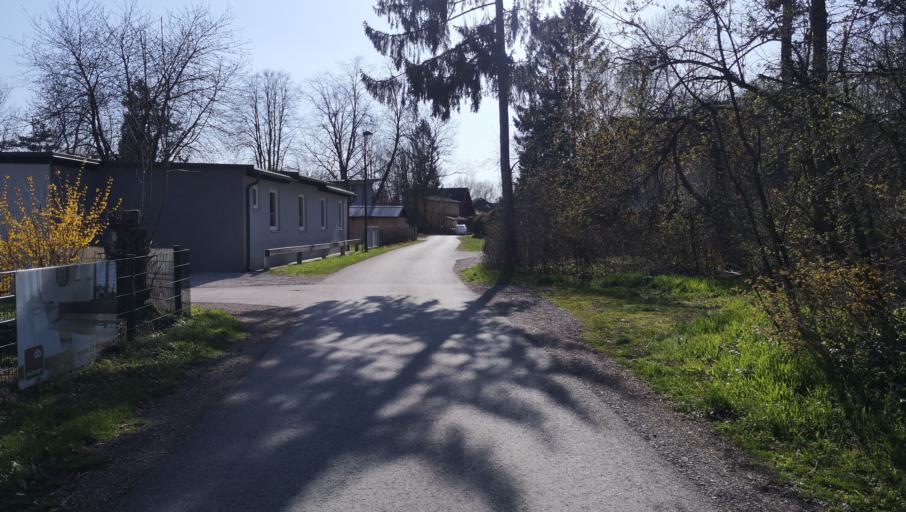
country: AT
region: Lower Austria
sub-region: Politischer Bezirk Melk
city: Blindenmarkt
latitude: 48.1181
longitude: 14.9878
